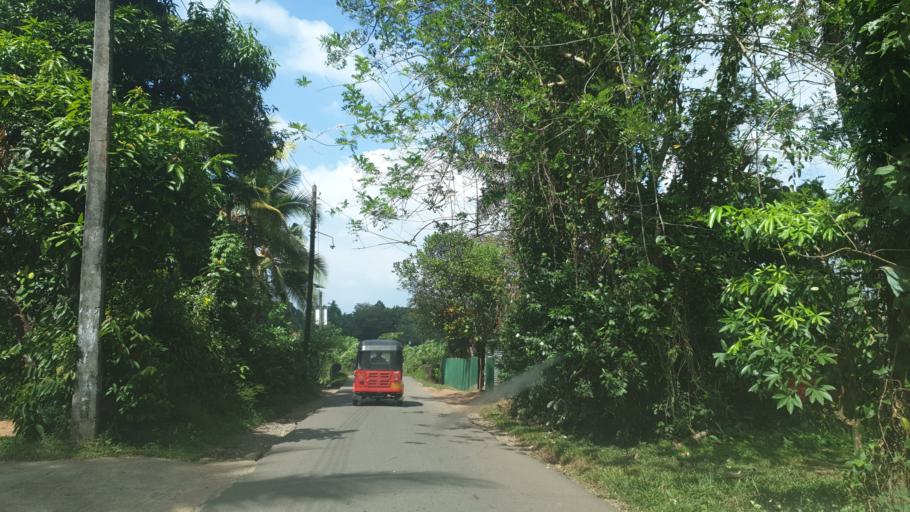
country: LK
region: Western
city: Horana South
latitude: 6.7012
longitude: 79.9860
